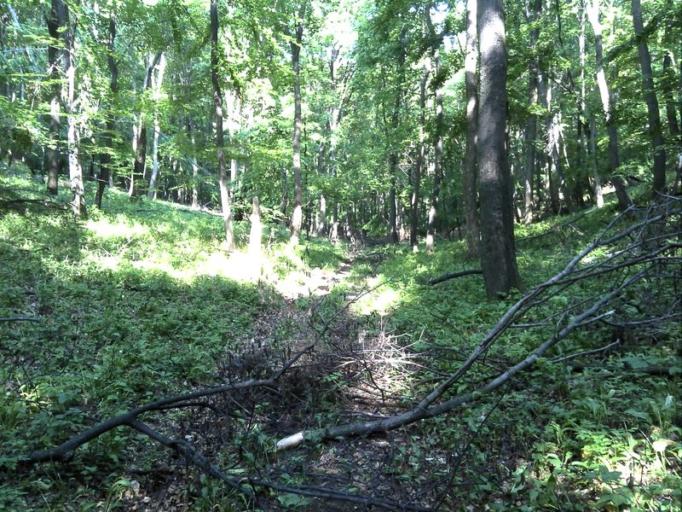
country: HU
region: Baranya
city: Pellerd
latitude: 46.1105
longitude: 18.1589
